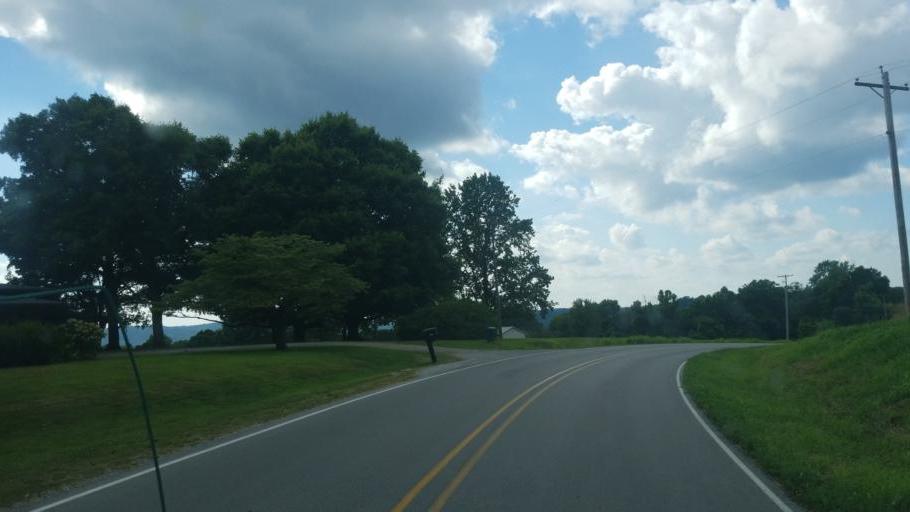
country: US
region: Illinois
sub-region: Union County
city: Cobden
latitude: 37.5479
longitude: -89.2941
